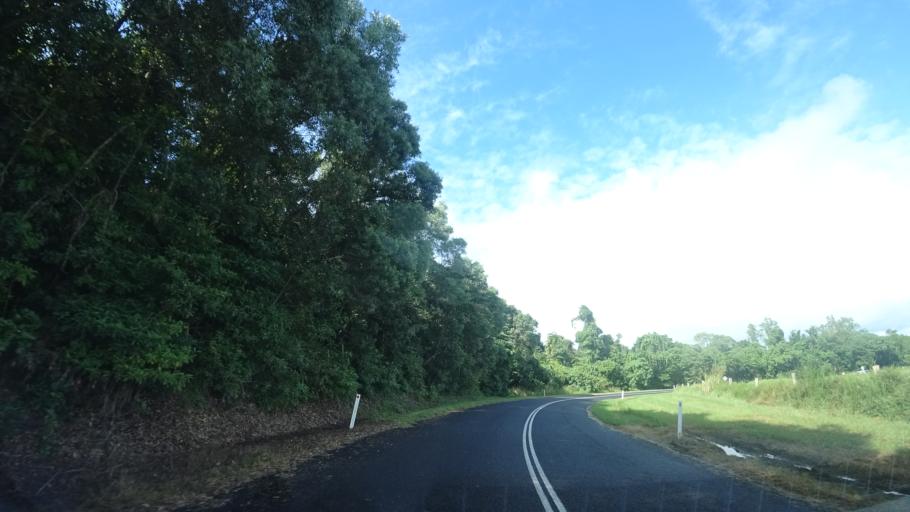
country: AU
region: Queensland
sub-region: Cassowary Coast
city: Innisfail
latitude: -17.5672
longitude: 146.0868
